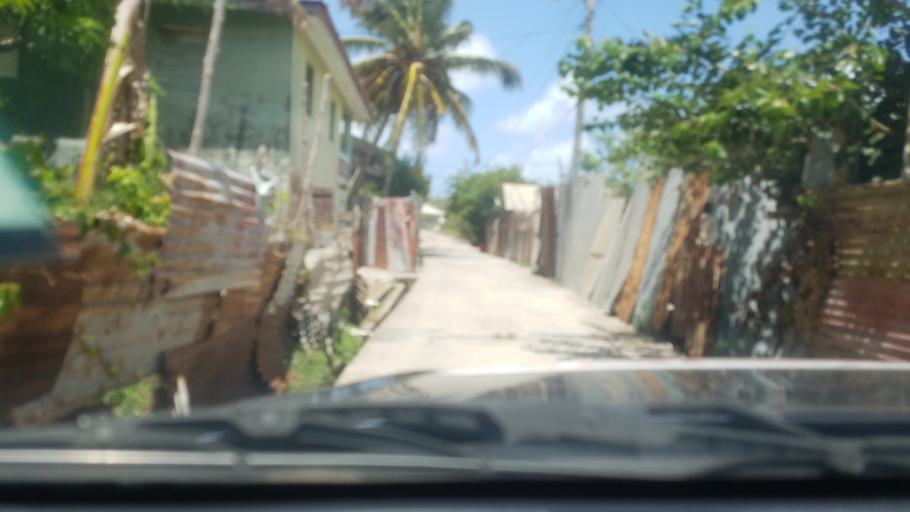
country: LC
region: Vieux-Fort
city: Vieux Fort
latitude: 13.7245
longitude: -60.9507
